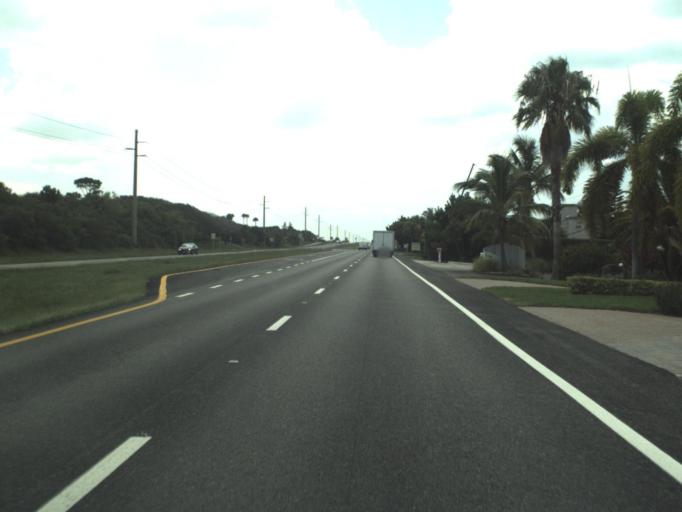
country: US
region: Florida
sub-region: Palm Beach County
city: Tequesta
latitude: 26.9861
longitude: -80.0925
